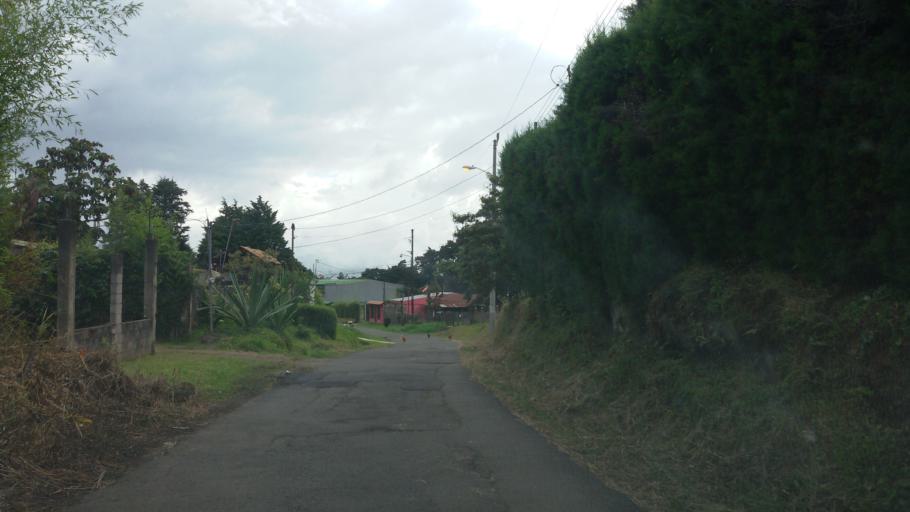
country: CR
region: Heredia
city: Angeles
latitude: 10.0331
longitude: -84.0195
